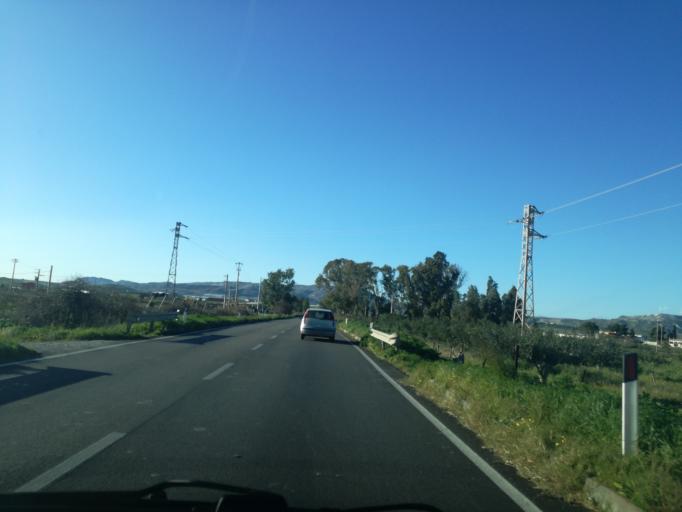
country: IT
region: Sicily
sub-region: Provincia di Caltanissetta
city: Butera
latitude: 37.1175
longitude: 14.1389
